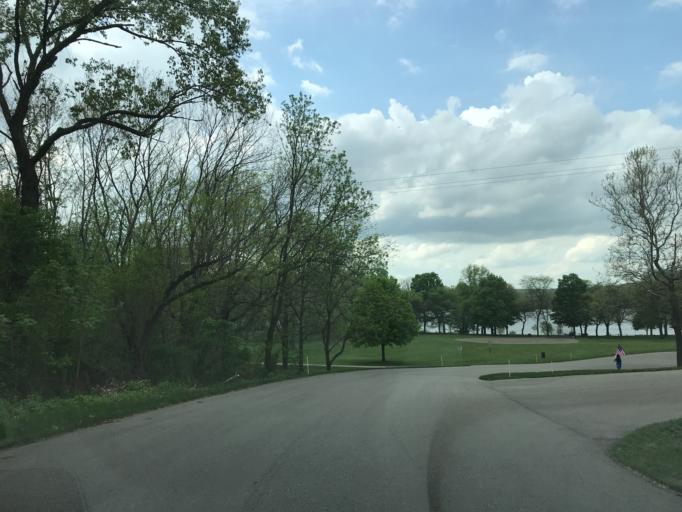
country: US
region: Michigan
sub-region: Oakland County
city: South Lyon
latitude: 42.5246
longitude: -83.6388
